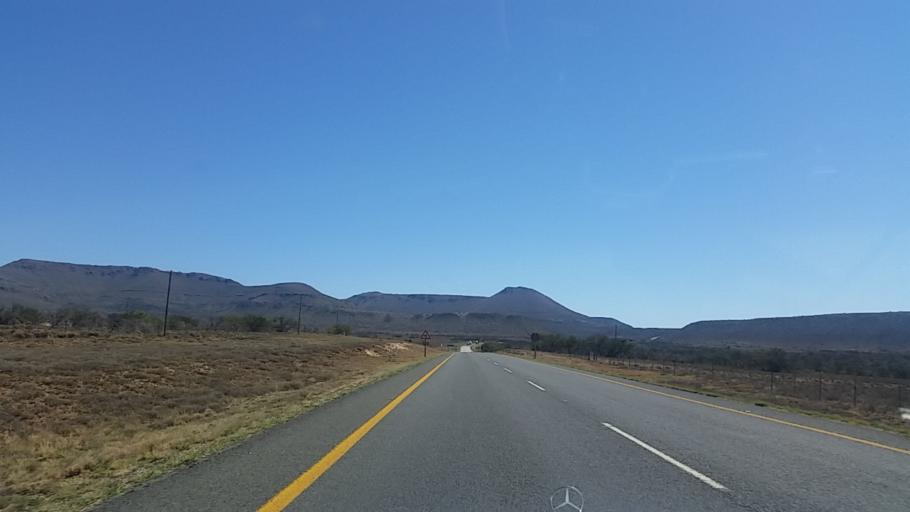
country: ZA
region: Eastern Cape
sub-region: Cacadu District Municipality
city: Graaff-Reinet
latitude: -32.0919
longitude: 24.6036
